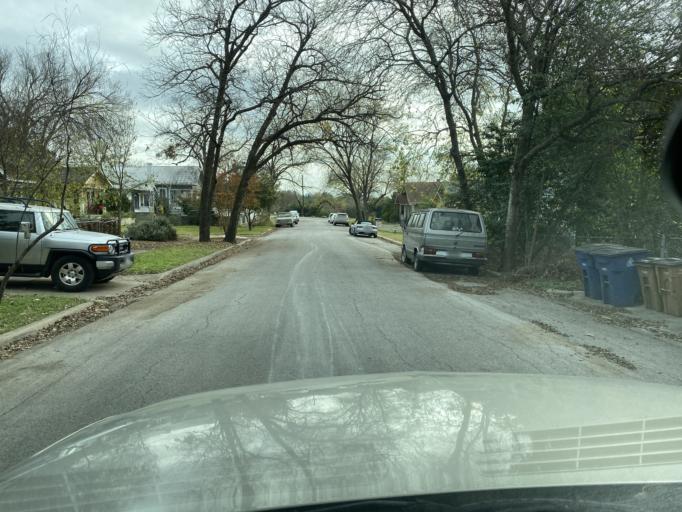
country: US
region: Texas
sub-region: Travis County
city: Austin
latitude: 30.3003
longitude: -97.7284
